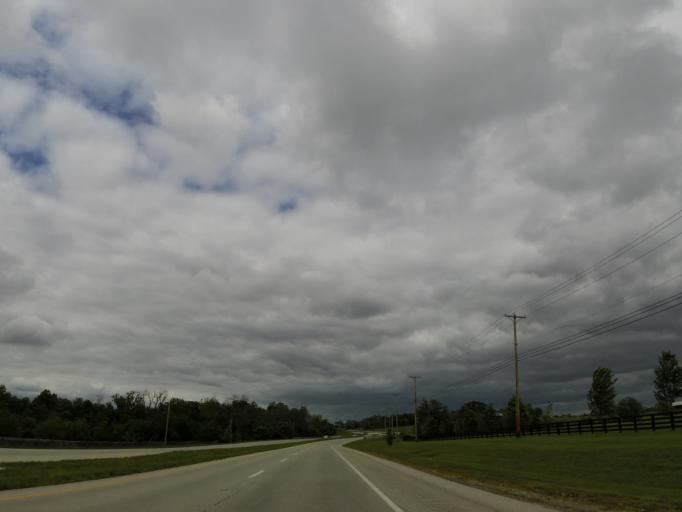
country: US
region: Kentucky
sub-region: Scott County
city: Georgetown
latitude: 38.1868
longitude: -84.5911
